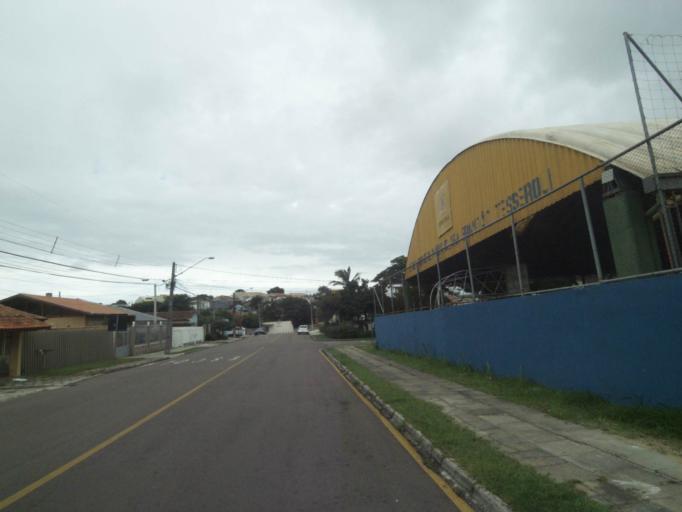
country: BR
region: Parana
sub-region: Curitiba
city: Curitiba
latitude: -25.4877
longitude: -49.2878
